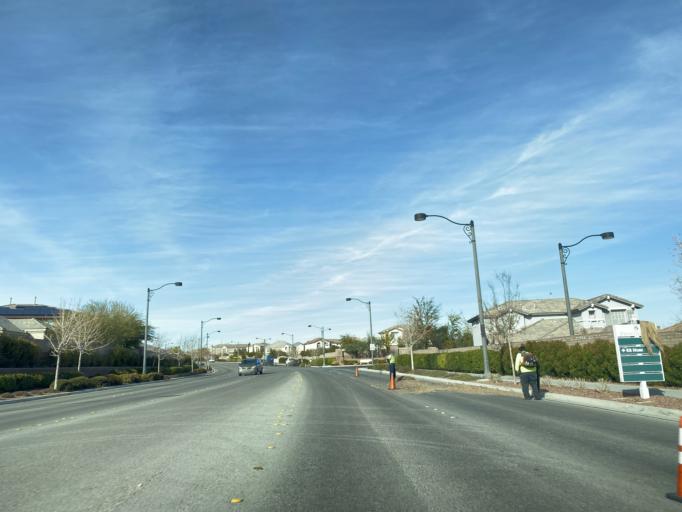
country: US
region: Nevada
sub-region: Clark County
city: Summerlin South
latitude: 36.3008
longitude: -115.3195
